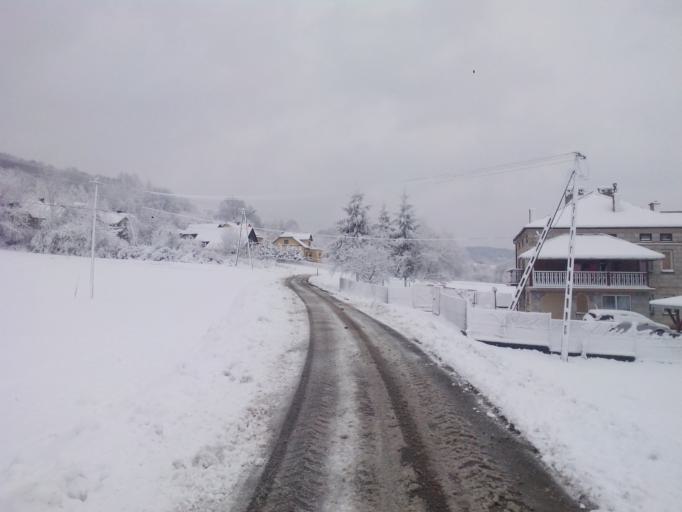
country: PL
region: Subcarpathian Voivodeship
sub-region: Powiat strzyzowski
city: Strzyzow
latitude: 49.8427
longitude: 21.8278
